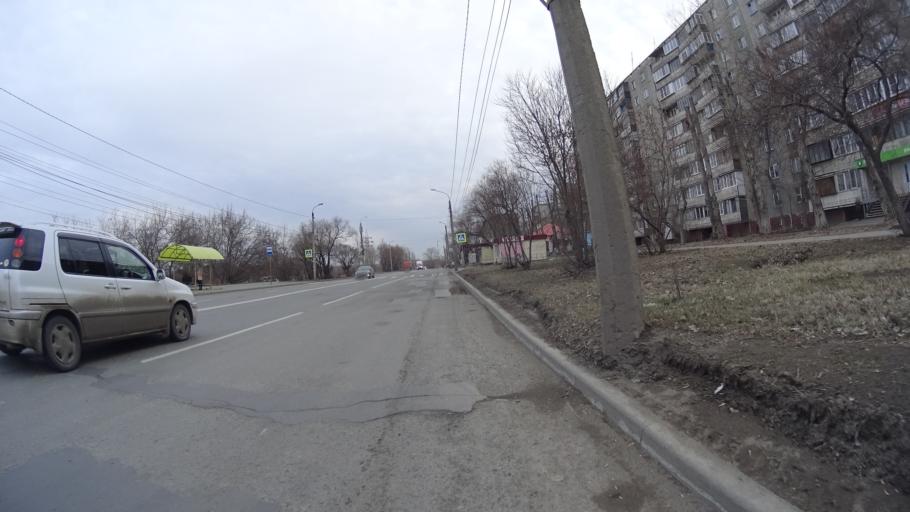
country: RU
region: Chelyabinsk
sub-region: Gorod Chelyabinsk
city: Chelyabinsk
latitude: 55.1816
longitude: 61.4869
